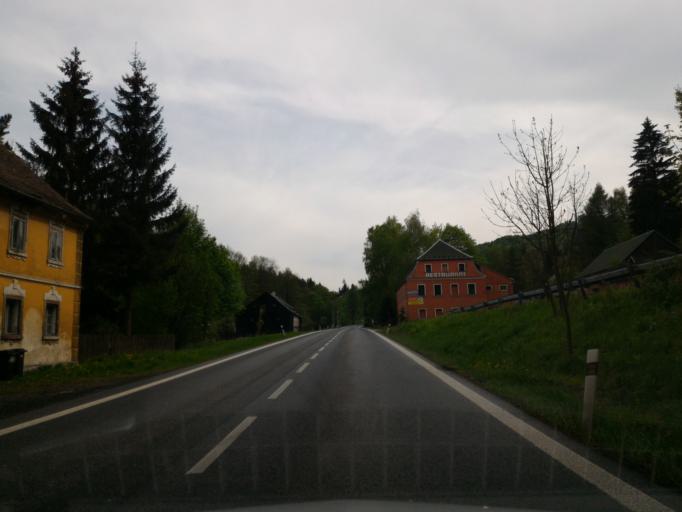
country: CZ
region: Ustecky
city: Dolni Podluzi
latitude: 50.8679
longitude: 14.5875
